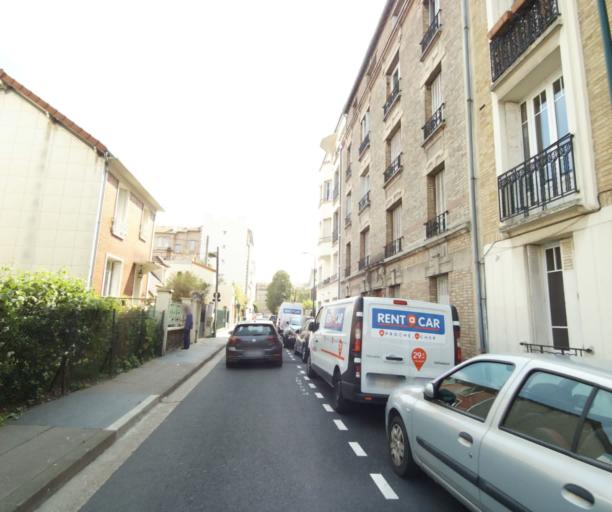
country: FR
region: Ile-de-France
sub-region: Departement des Hauts-de-Seine
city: La Garenne-Colombes
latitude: 48.9106
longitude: 2.2387
